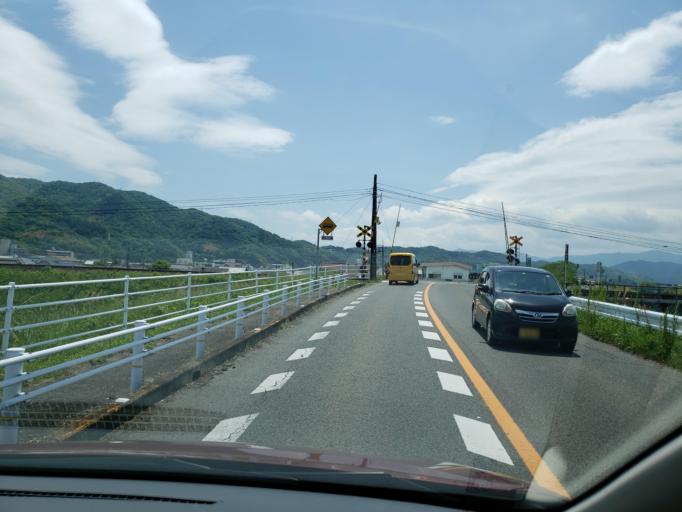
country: JP
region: Tokushima
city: Tokushima-shi
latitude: 34.0771
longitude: 134.5020
